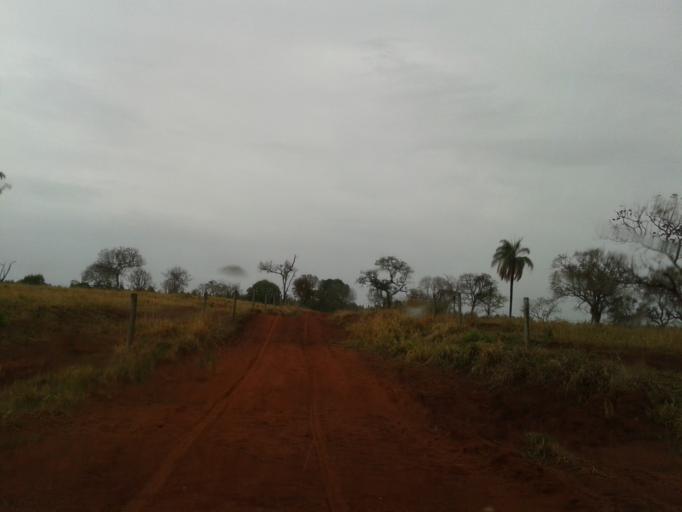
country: BR
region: Minas Gerais
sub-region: Campina Verde
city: Campina Verde
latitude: -19.3471
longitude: -49.5504
